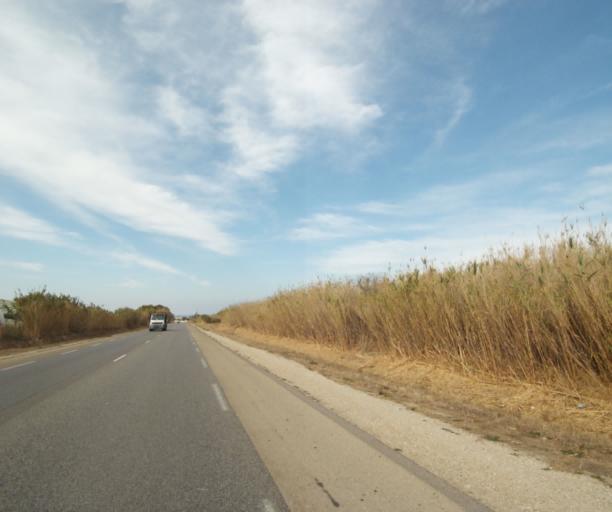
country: FR
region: Provence-Alpes-Cote d'Azur
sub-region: Departement des Bouches-du-Rhone
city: Gignac-la-Nerthe
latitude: 43.3889
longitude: 5.2121
